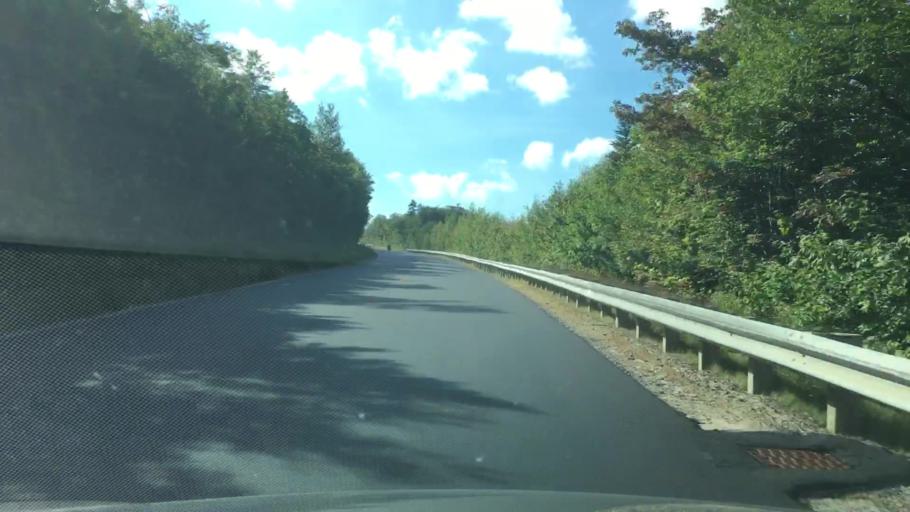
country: US
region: New Hampshire
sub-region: Grafton County
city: Woodstock
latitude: 44.0227
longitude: -71.4689
